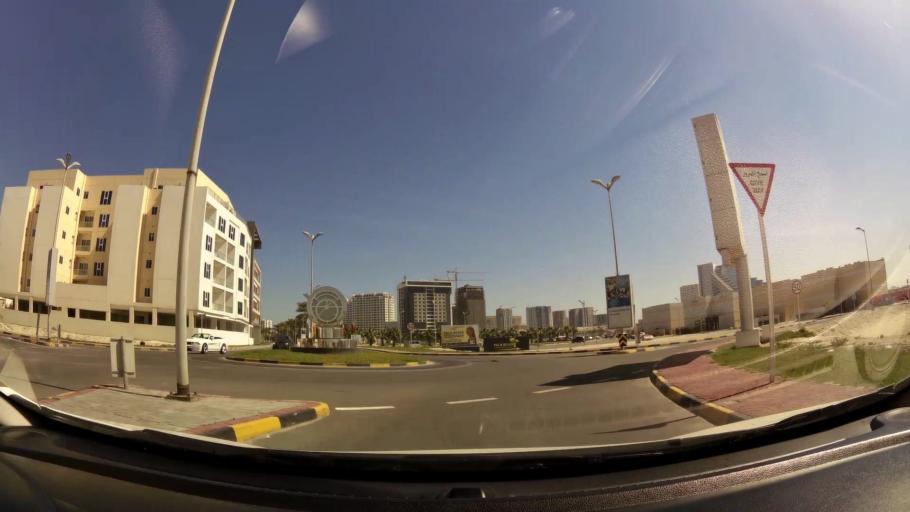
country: BH
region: Muharraq
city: Al Hadd
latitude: 26.2944
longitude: 50.6593
